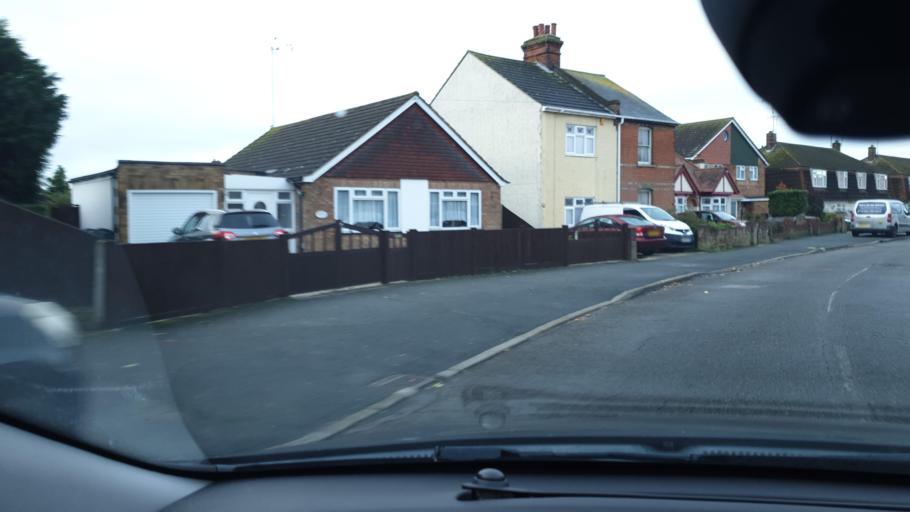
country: GB
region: England
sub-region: Essex
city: Clacton-on-Sea
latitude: 51.7933
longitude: 1.1386
